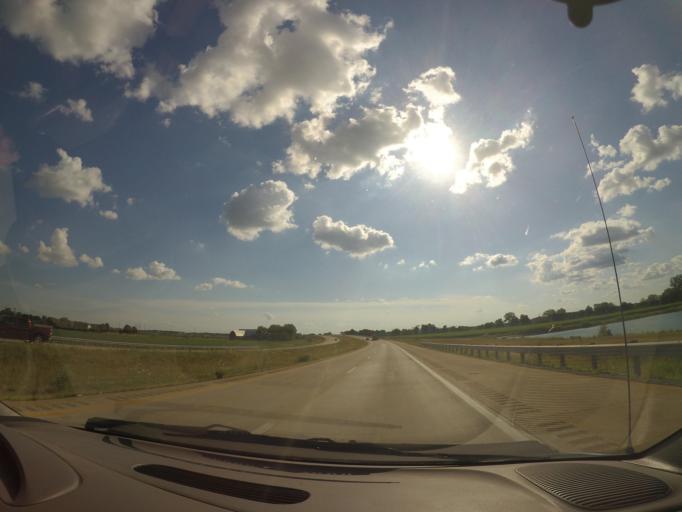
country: US
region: Ohio
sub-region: Lucas County
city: Waterville
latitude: 41.5242
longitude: -83.7355
